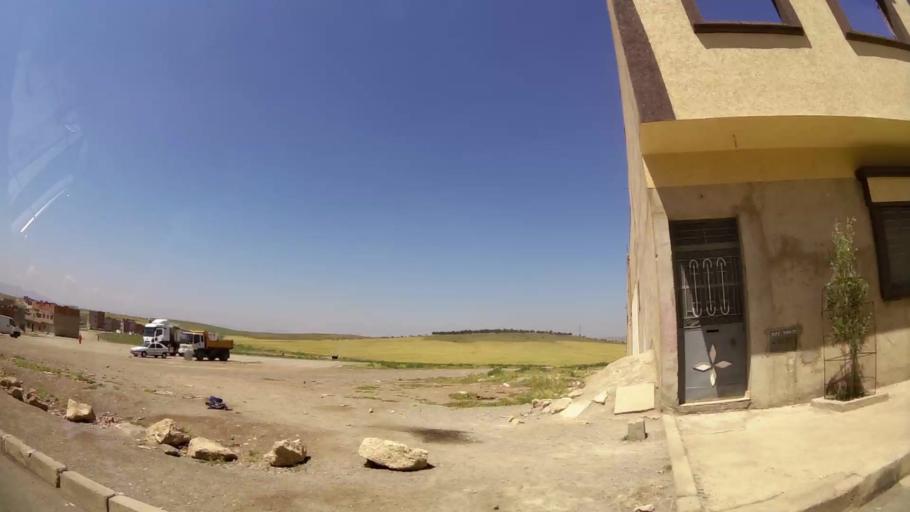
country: MA
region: Oriental
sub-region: Oujda-Angad
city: Oujda
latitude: 34.6819
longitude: -1.9586
